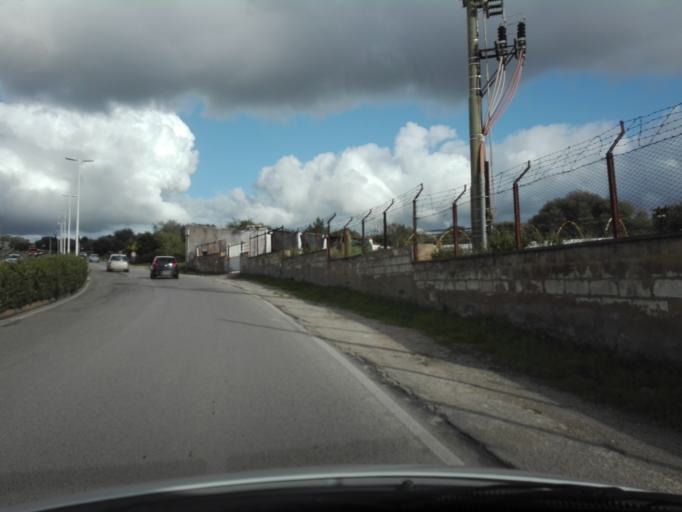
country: IT
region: Sardinia
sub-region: Provincia di Sassari
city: Sassari
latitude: 40.7107
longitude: 8.5724
